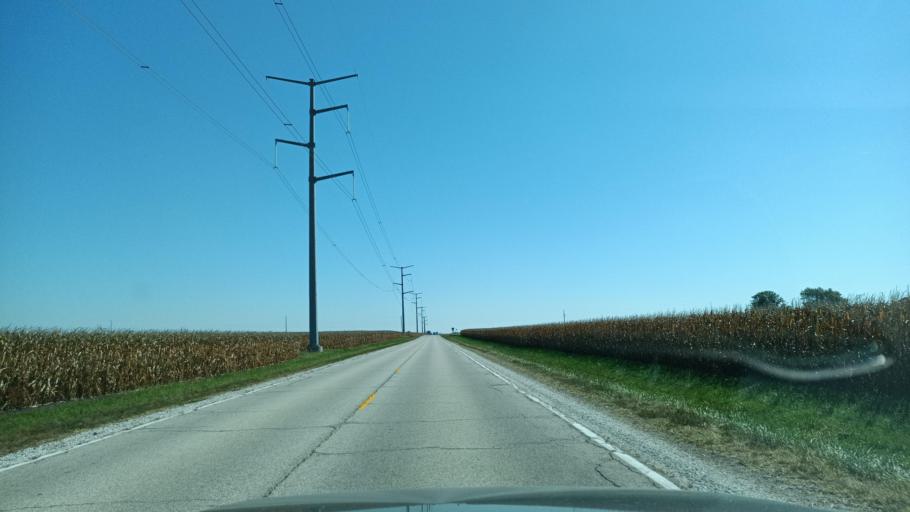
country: US
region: Illinois
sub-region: Peoria County
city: Elmwood
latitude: 40.9023
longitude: -89.9894
